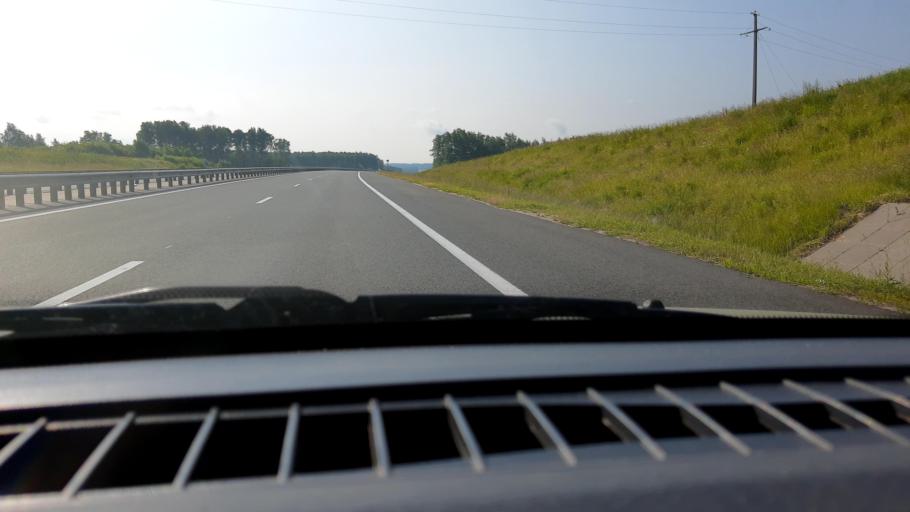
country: RU
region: Nizjnij Novgorod
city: Kstovo
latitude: 56.0921
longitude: 44.0796
